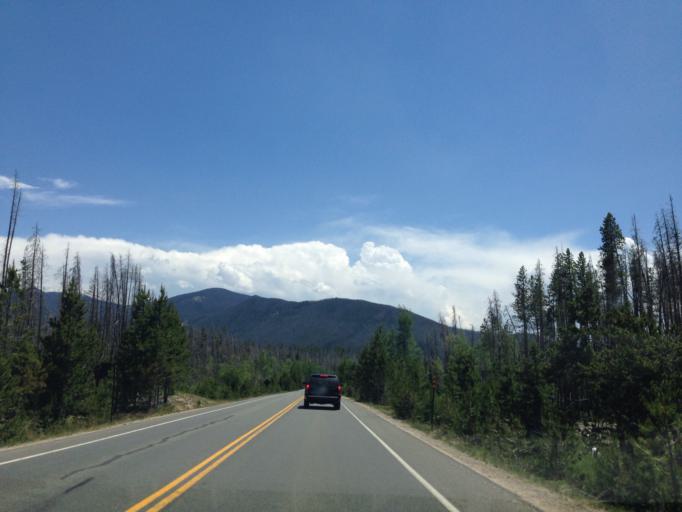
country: US
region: Colorado
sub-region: Grand County
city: Granby
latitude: 40.2643
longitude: -105.8324
